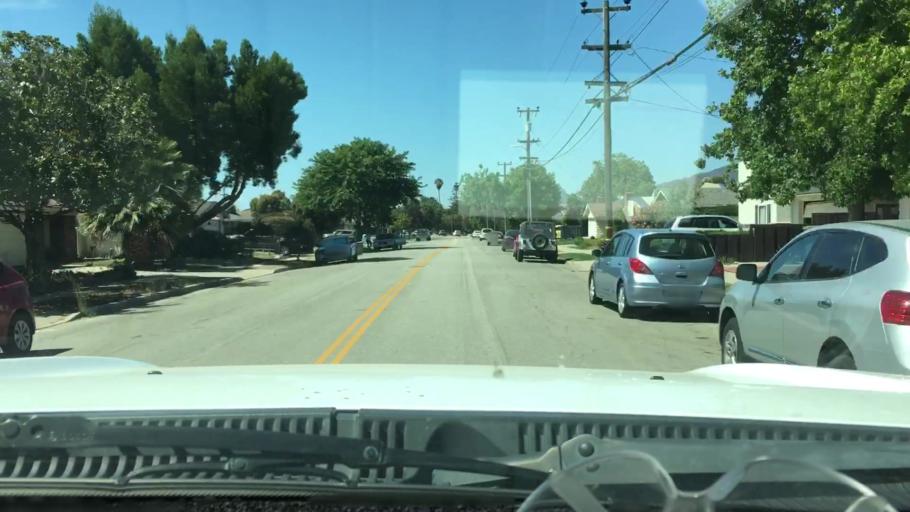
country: US
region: California
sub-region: San Luis Obispo County
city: San Luis Obispo
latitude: 35.2608
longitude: -120.6850
